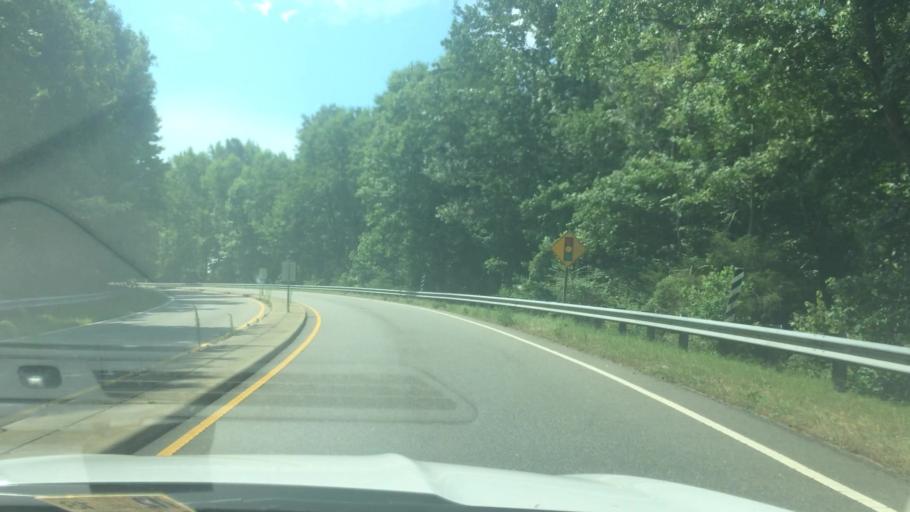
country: US
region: Virginia
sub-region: City of Poquoson
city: Poquoson
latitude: 37.1285
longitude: -76.4602
